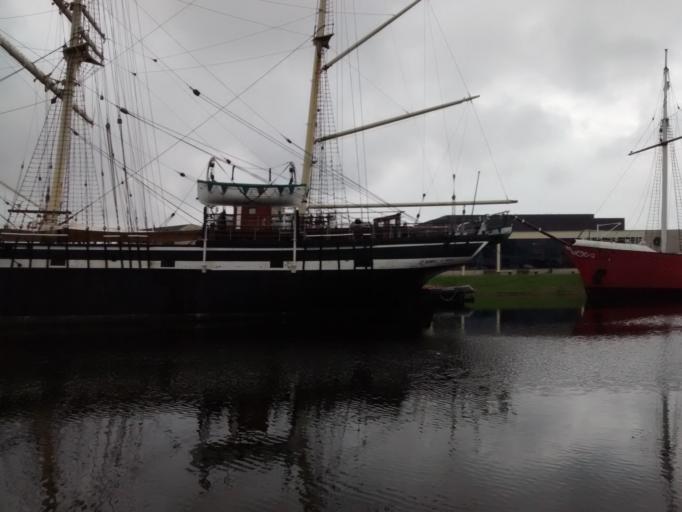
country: DE
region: Bremen
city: Bremerhaven
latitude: 53.5411
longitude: 8.5788
